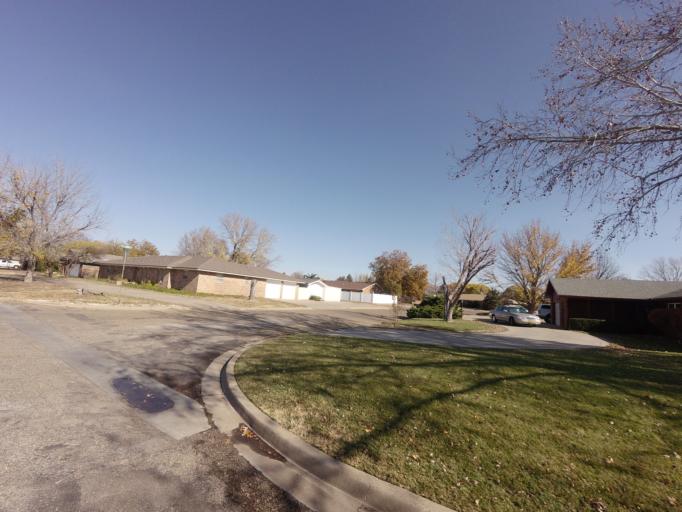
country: US
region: New Mexico
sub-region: Curry County
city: Clovis
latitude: 34.4142
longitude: -103.1818
